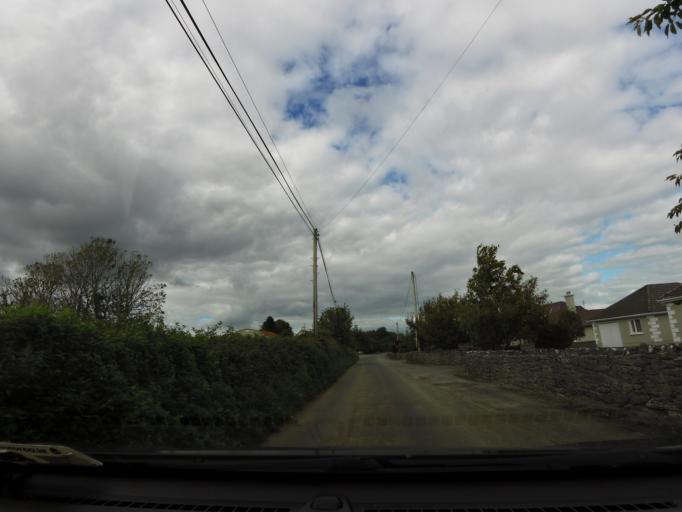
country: IE
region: Connaught
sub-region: County Galway
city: Moycullen
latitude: 53.3230
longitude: -9.1442
